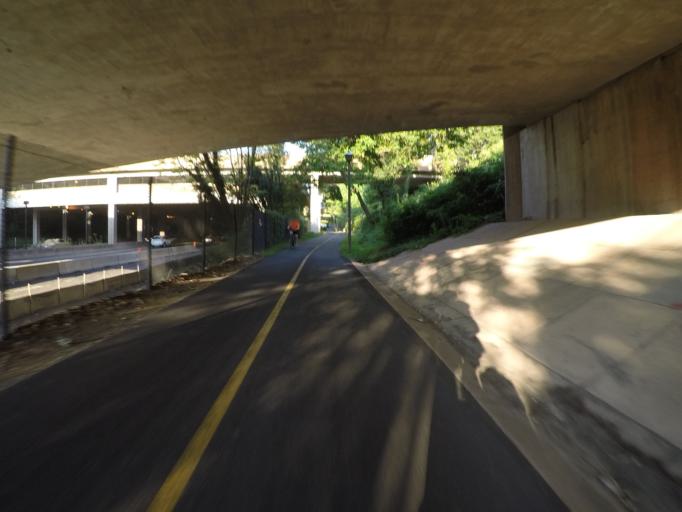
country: US
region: Virginia
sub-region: Arlington County
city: Arlington
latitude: 38.8899
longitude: -77.1083
